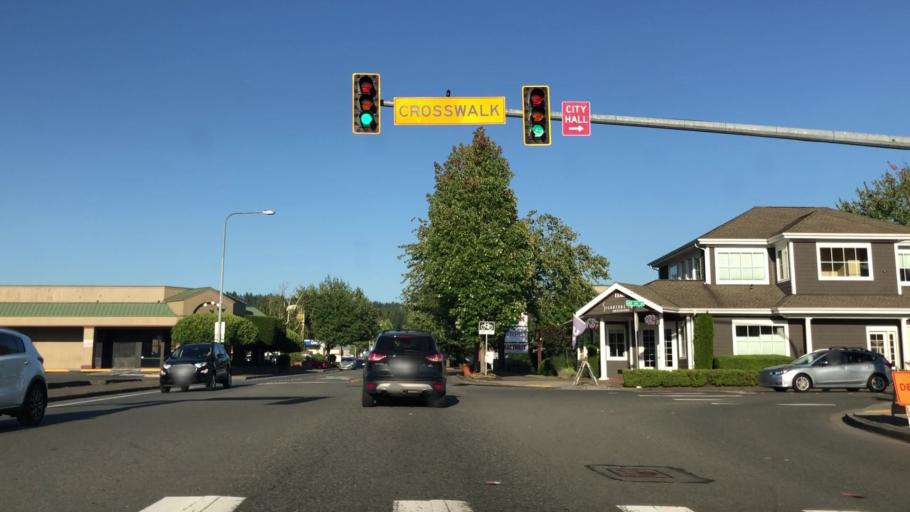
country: US
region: Washington
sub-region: King County
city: Woodinville
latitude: 47.7545
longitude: -122.1624
